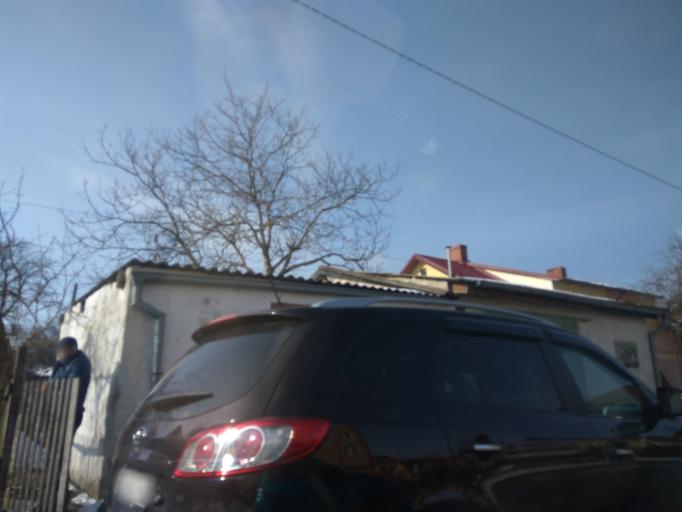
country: RU
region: Kaliningrad
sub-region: Zelenogradskiy Rayon
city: Zelenogradsk
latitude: 54.9584
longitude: 20.4865
